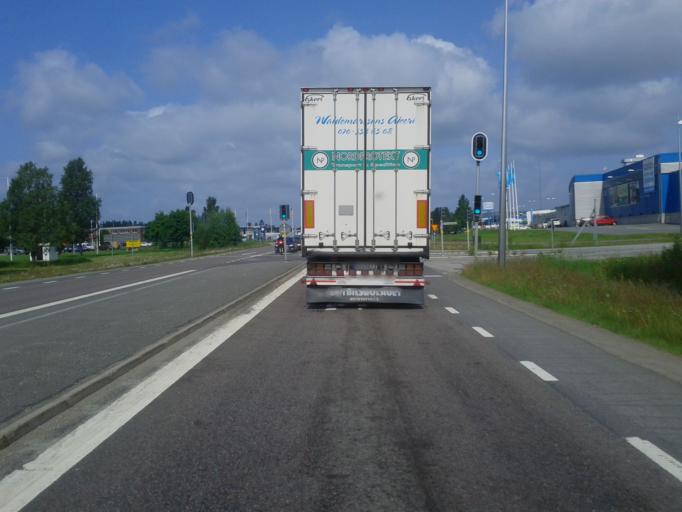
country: SE
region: Vaesterbotten
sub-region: Skelleftea Kommun
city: Skelleftea
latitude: 64.7352
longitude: 20.9682
